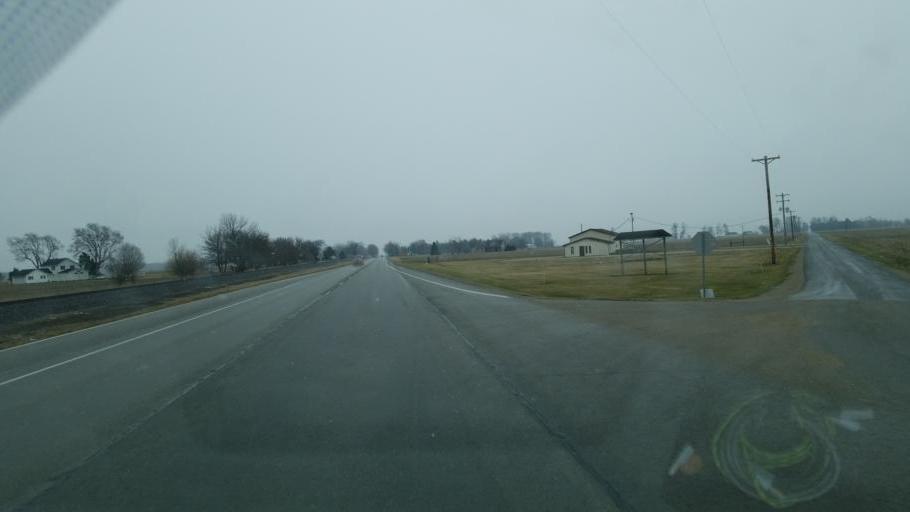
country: US
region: Indiana
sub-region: Wabash County
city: Wabash
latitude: 40.7569
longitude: -85.8097
